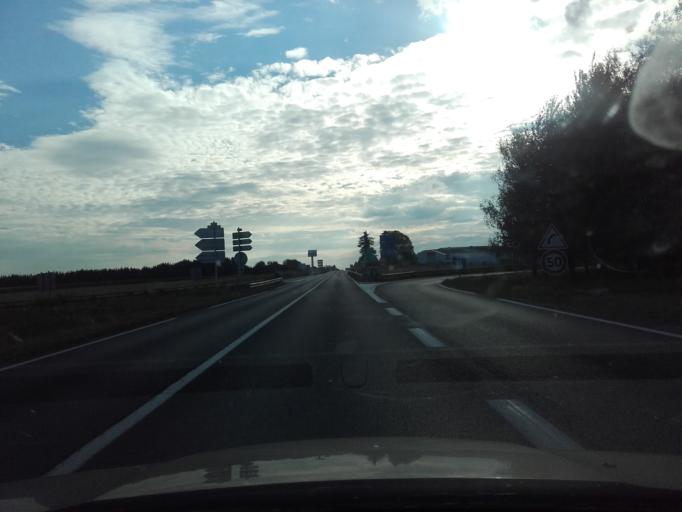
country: FR
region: Centre
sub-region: Departement d'Indre-et-Loire
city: Parcay-Meslay
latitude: 47.4535
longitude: 0.7326
